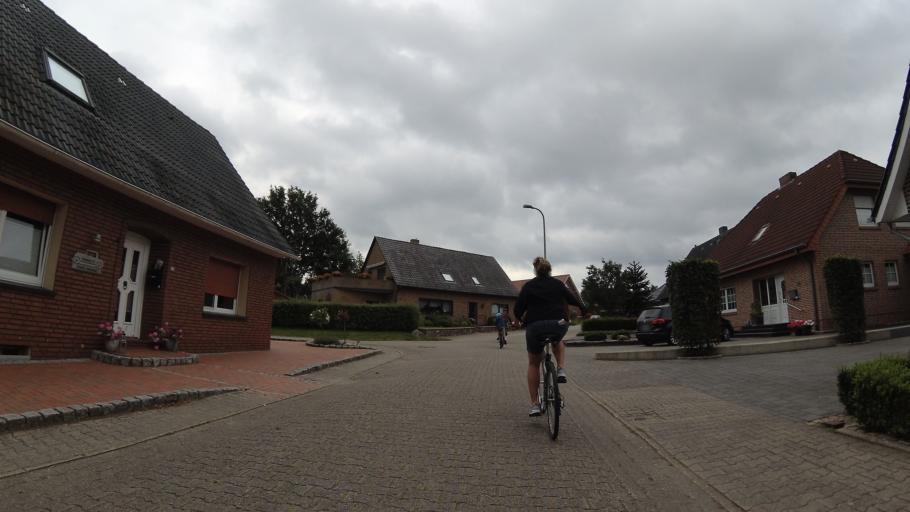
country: DE
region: Lower Saxony
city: Lathen
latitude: 52.8645
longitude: 7.3115
